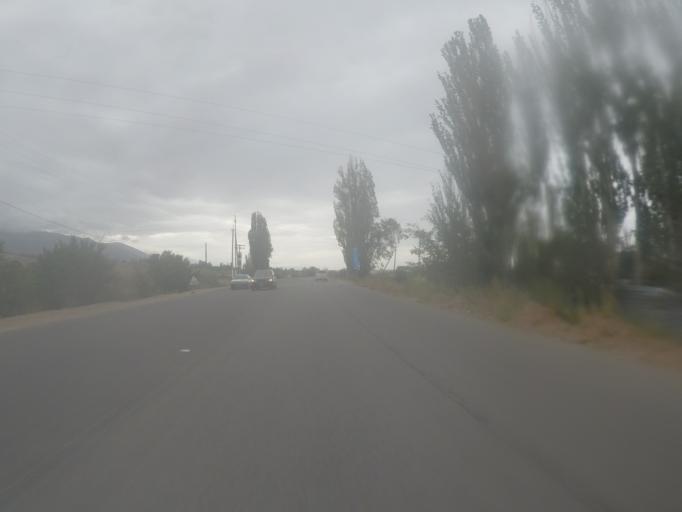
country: KG
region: Ysyk-Koel
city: Cholpon-Ata
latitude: 42.6765
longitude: 77.3063
